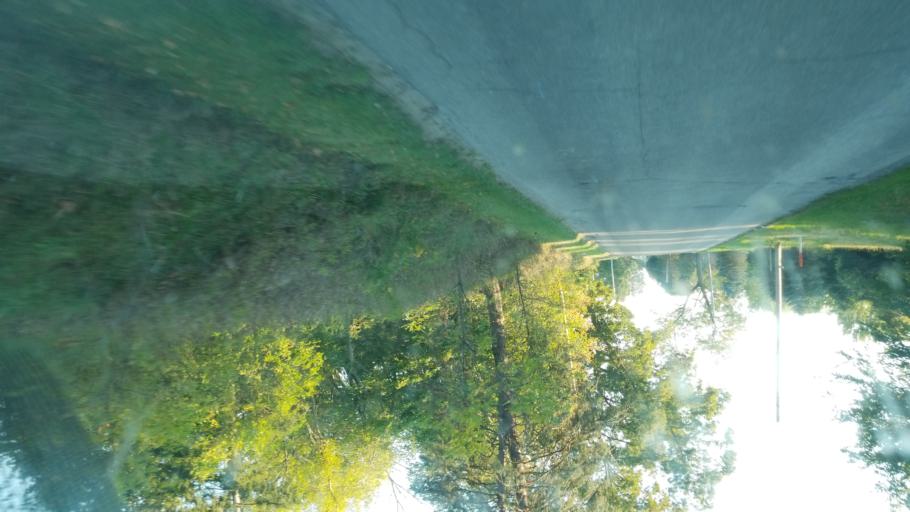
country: US
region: Indiana
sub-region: LaGrange County
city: Lagrange
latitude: 41.6377
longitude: -85.4248
